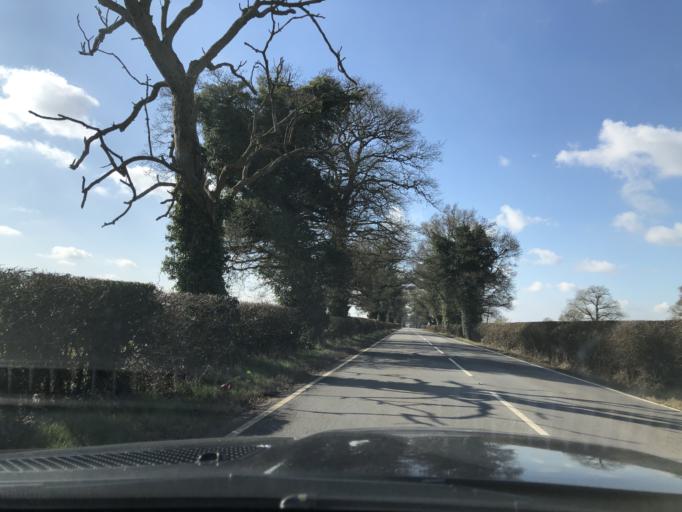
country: GB
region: England
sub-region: Warwickshire
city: Wolston
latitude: 52.3411
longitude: -1.3509
